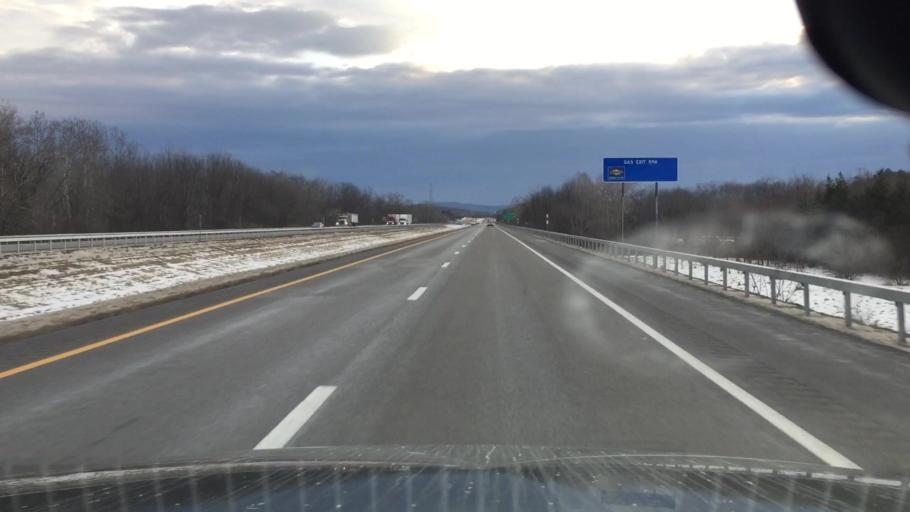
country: US
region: Pennsylvania
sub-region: Bradford County
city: South Waverly
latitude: 42.0008
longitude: -76.6017
